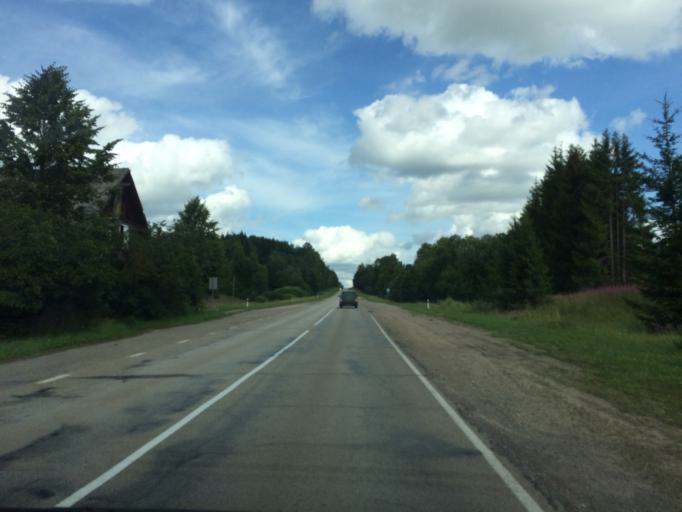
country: LV
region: Rezekne
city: Rezekne
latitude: 56.5916
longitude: 27.4114
